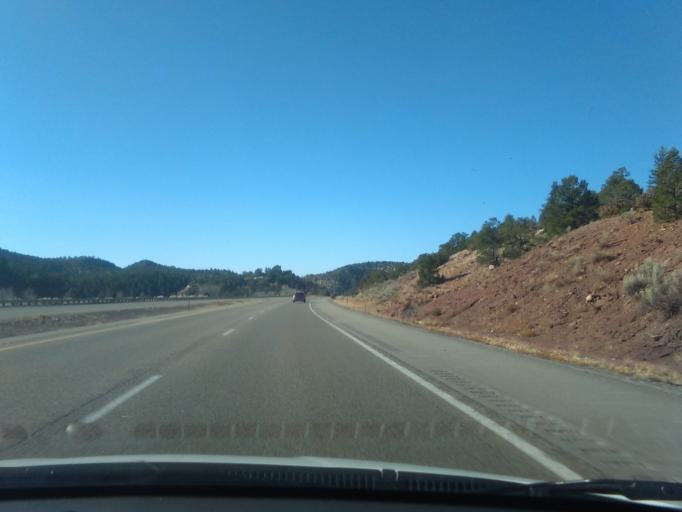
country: US
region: New Mexico
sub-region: San Miguel County
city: Pecos
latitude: 35.5630
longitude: -105.8055
